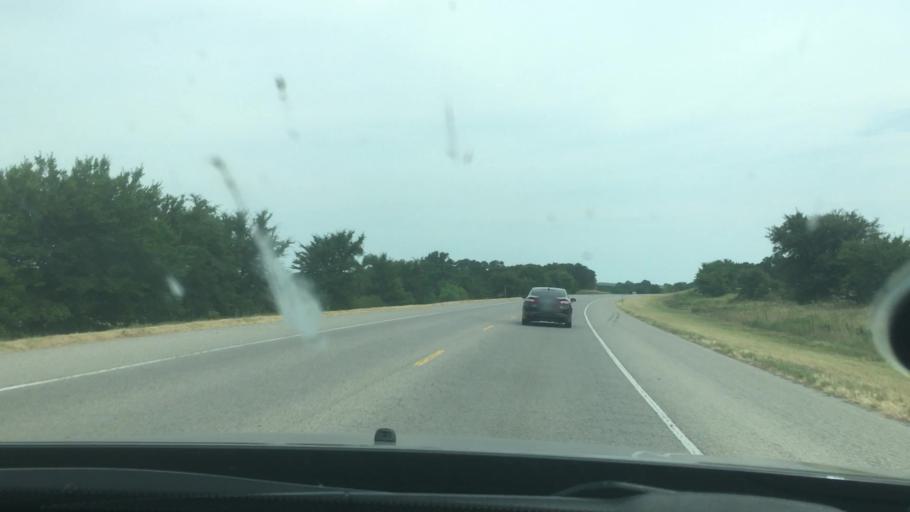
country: US
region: Oklahoma
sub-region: Pontotoc County
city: Ada
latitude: 34.6897
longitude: -96.5953
